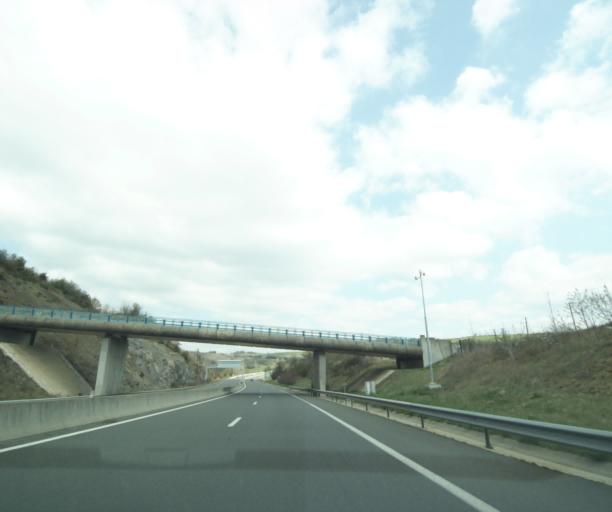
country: FR
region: Languedoc-Roussillon
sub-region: Departement de la Lozere
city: Chirac
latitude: 44.5329
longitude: 3.2513
